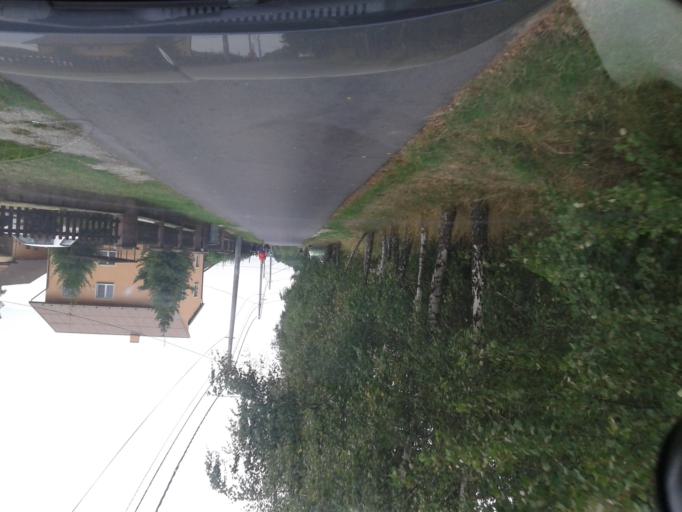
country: CZ
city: Dolni Lutyne
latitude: 49.8849
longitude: 18.4424
